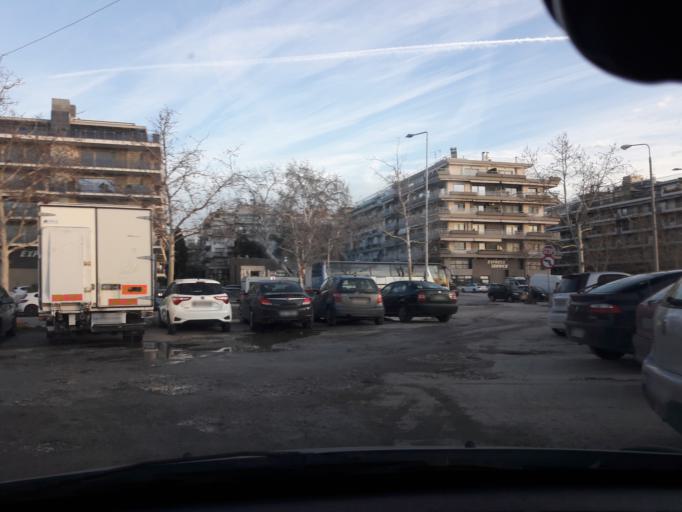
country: GR
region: Central Macedonia
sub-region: Nomos Thessalonikis
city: Kalamaria
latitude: 40.5946
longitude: 22.9494
